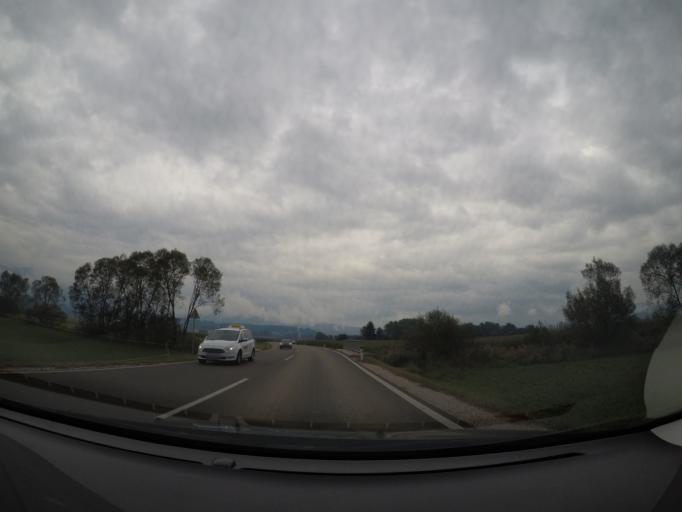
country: AT
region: Styria
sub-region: Politischer Bezirk Murtal
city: Spielberg bei Knittelfeld
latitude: 47.2039
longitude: 14.7831
